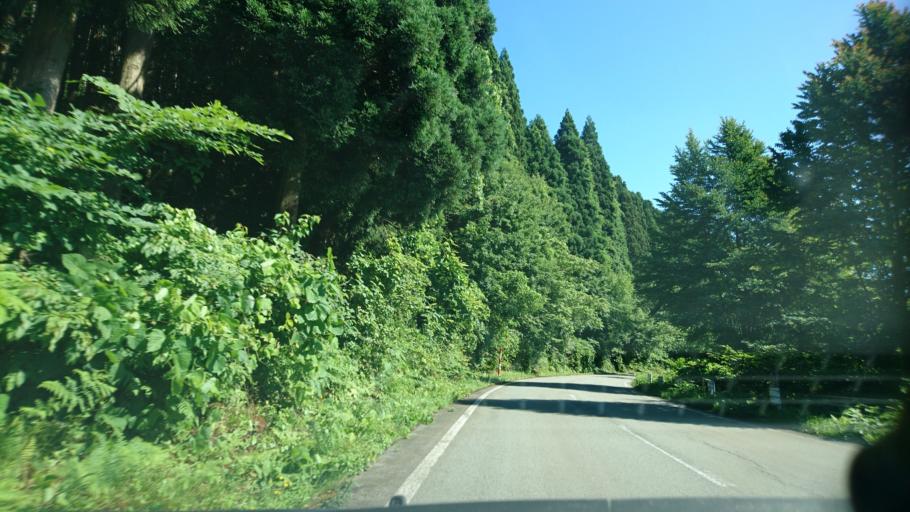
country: JP
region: Akita
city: Kakunodatemachi
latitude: 39.7370
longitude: 140.6328
